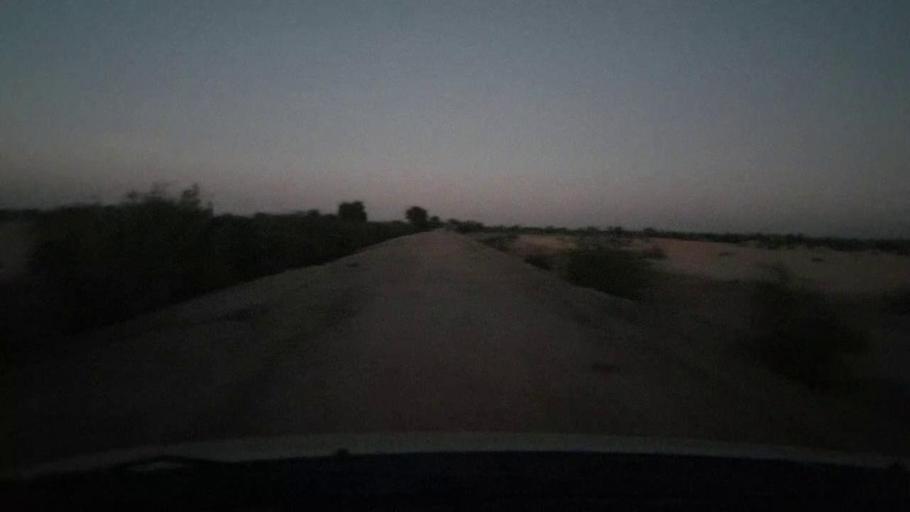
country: PK
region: Sindh
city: Phulji
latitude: 26.9017
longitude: 67.4765
